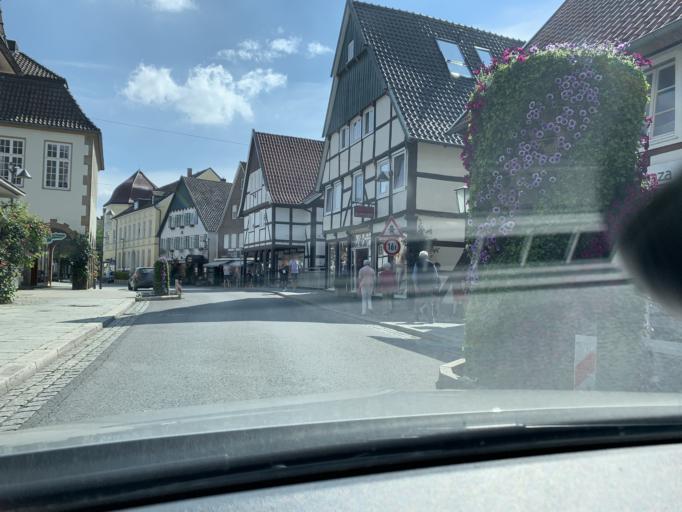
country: DE
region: North Rhine-Westphalia
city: Rietberg
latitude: 51.8103
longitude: 8.4279
